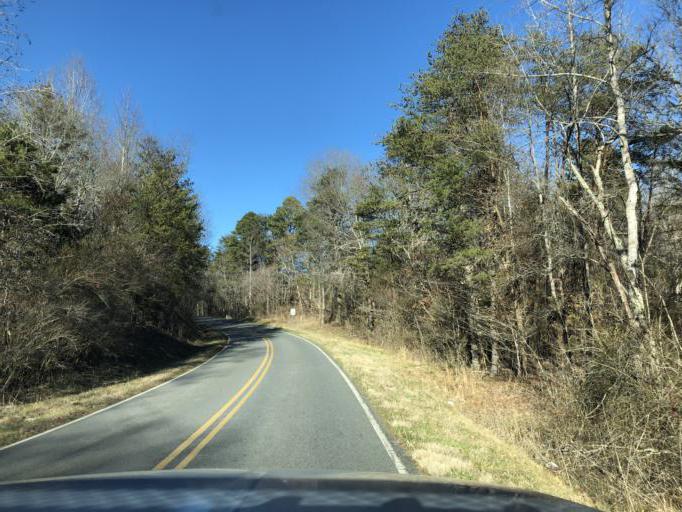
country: US
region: North Carolina
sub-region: Cleveland County
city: Shelby
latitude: 35.3305
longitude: -81.5397
